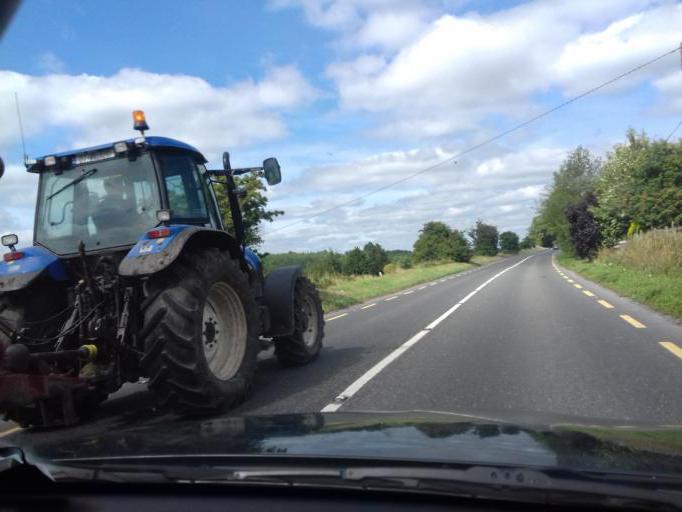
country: IE
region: Leinster
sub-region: Wicklow
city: Valleymount
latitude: 53.0466
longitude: -6.6338
